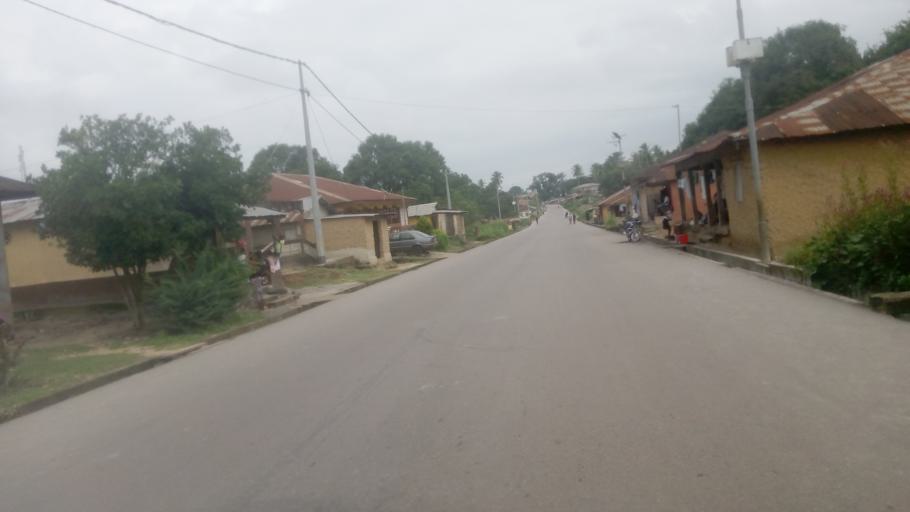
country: SL
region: Northern Province
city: Lunsar
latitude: 8.6896
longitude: -12.5364
